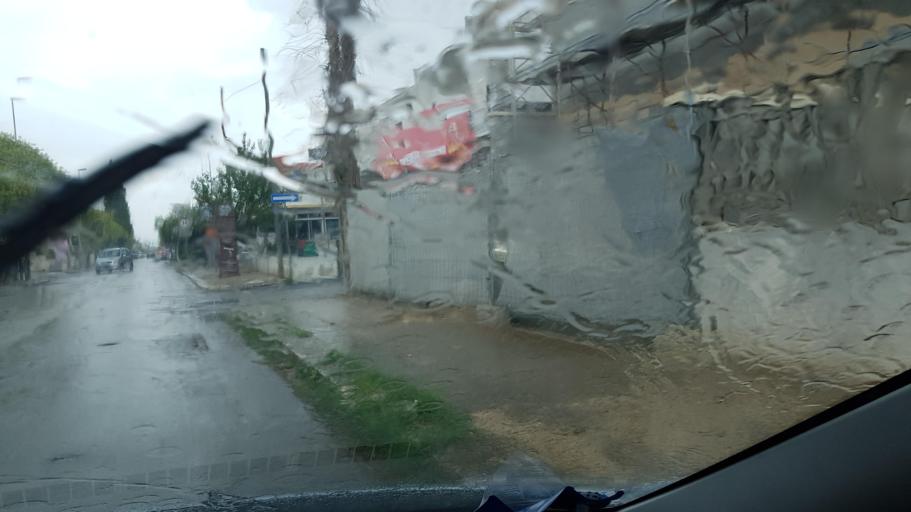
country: IT
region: Apulia
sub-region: Provincia di Lecce
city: Taurisano
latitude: 39.9569
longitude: 18.2200
